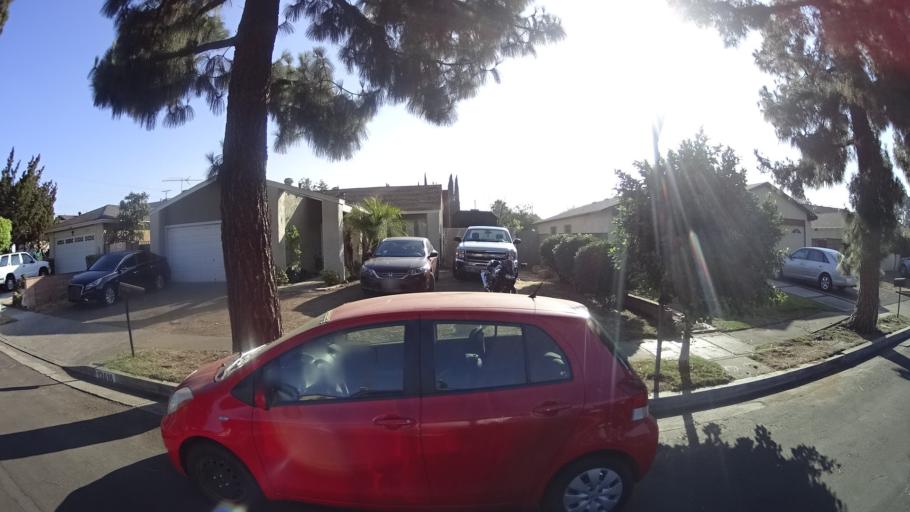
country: US
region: California
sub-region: Los Angeles County
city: Van Nuys
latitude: 34.2312
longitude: -118.4180
